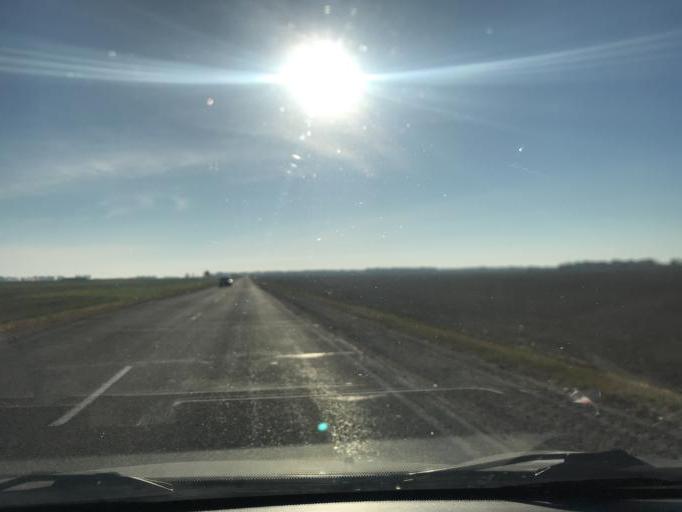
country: BY
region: Gomel
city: Brahin
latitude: 51.8105
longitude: 30.1046
